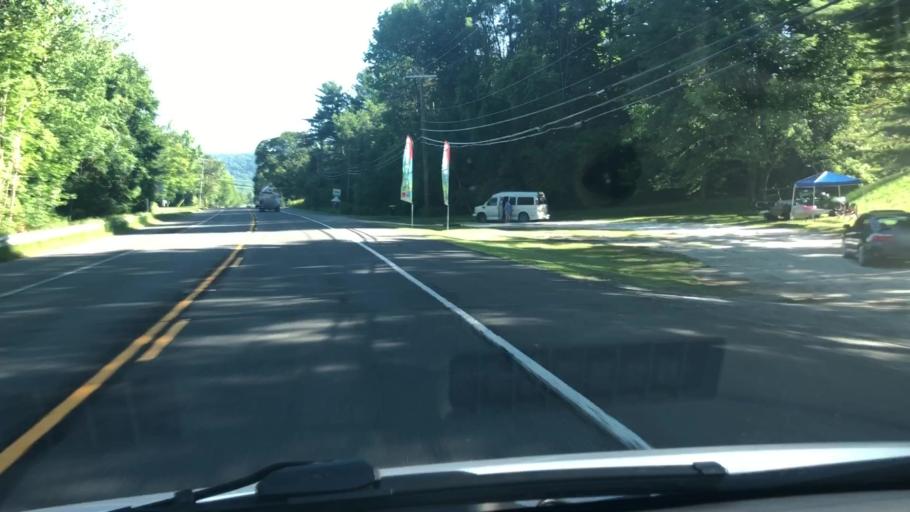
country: US
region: Massachusetts
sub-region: Berkshire County
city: Lanesborough
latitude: 42.5109
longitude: -73.1926
